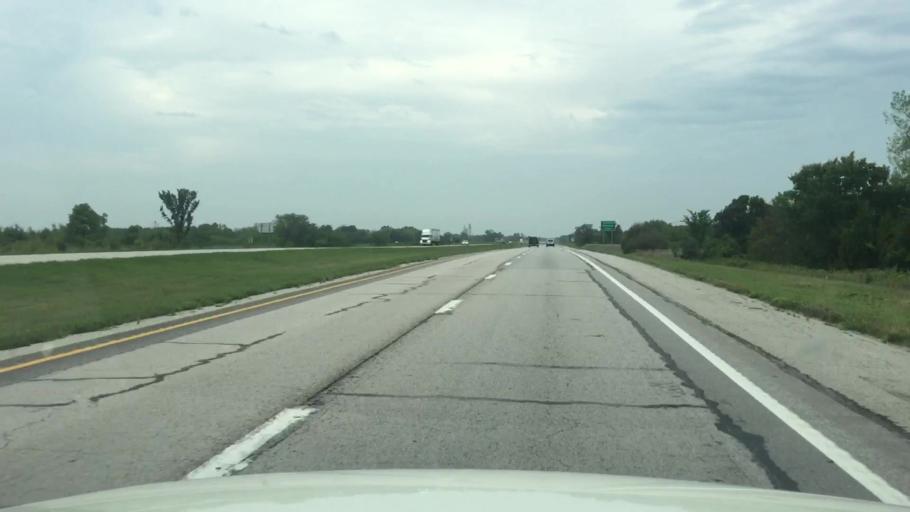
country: US
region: Missouri
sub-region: Harrison County
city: Bethany
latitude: 40.1353
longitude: -94.0479
